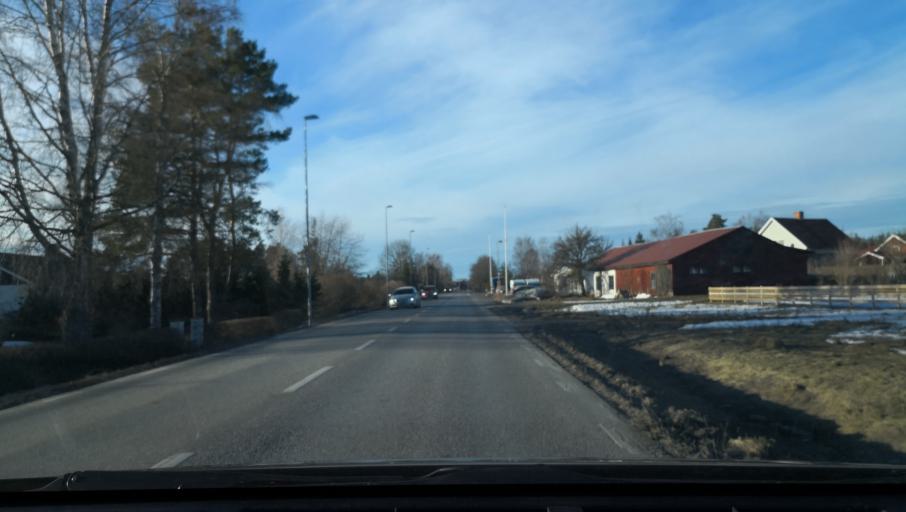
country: SE
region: Uppsala
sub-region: Osthammars Kommun
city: OEsthammar
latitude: 60.2830
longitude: 18.2934
